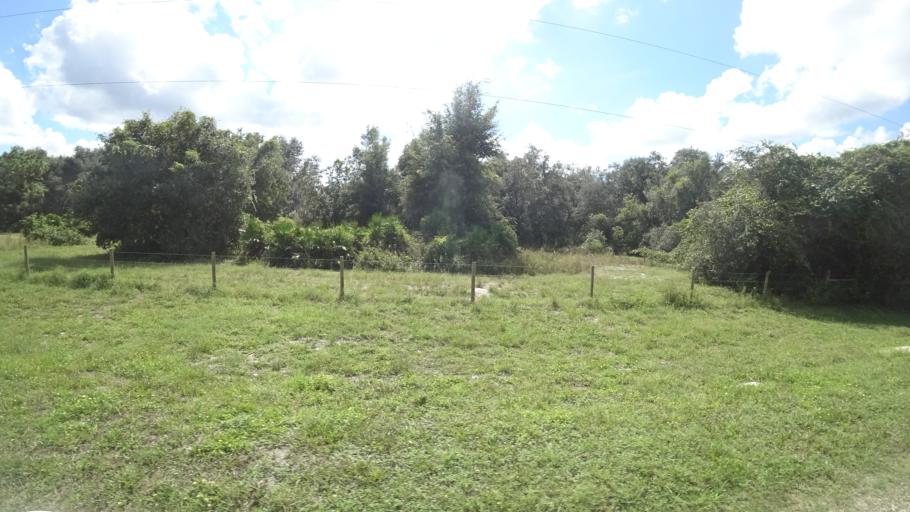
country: US
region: Florida
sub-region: Sarasota County
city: Lake Sarasota
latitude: 27.3205
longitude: -82.2588
